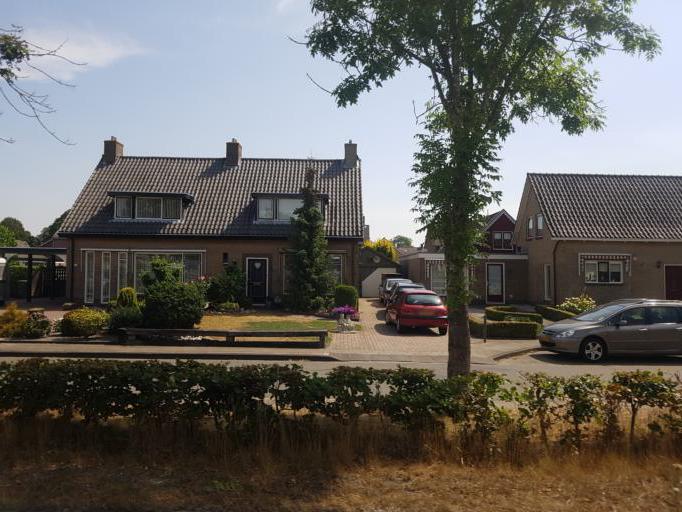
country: NL
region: Overijssel
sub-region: Gemeente Steenwijkerland
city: Giethoorn
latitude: 52.7398
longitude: 6.0772
